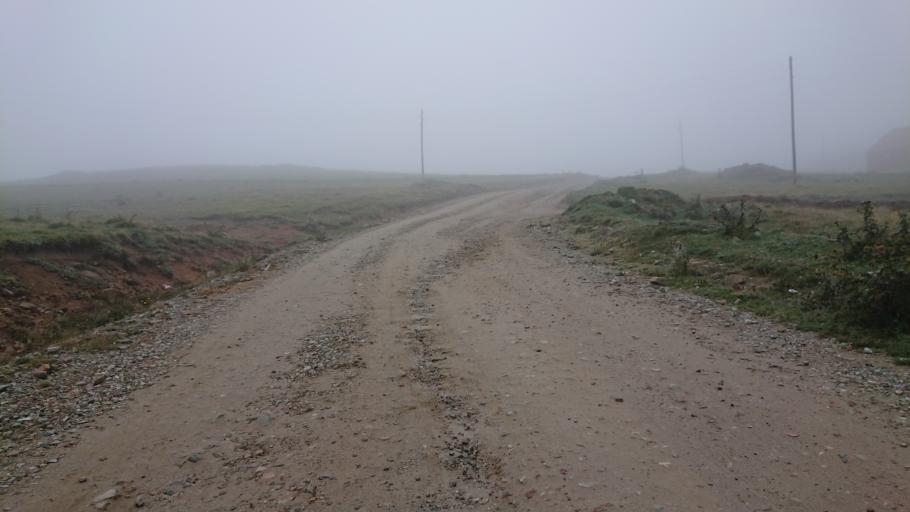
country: TR
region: Gumushane
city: Kurtun
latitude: 40.6724
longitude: 38.9935
